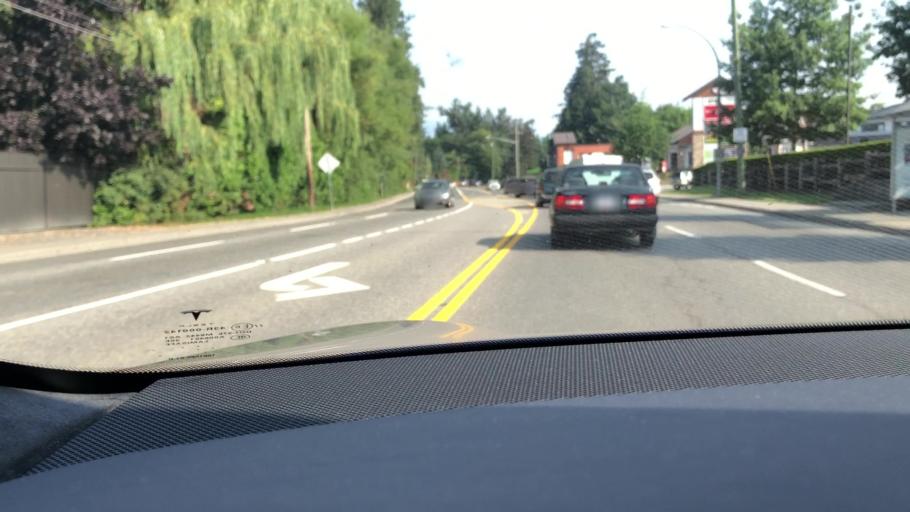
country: CA
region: British Columbia
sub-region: Fraser Valley Regional District
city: Chilliwack
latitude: 49.1231
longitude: -121.9599
